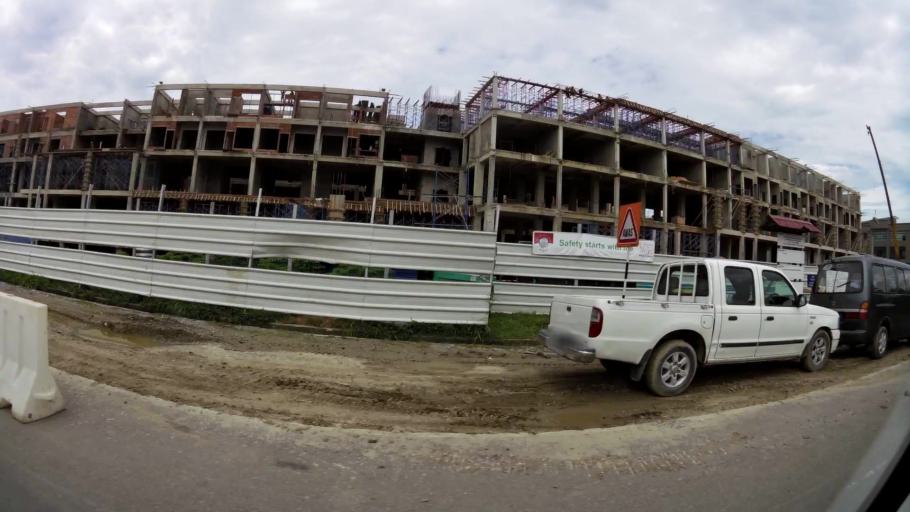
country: BN
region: Brunei and Muara
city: Bandar Seri Begawan
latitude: 4.8886
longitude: 114.8975
